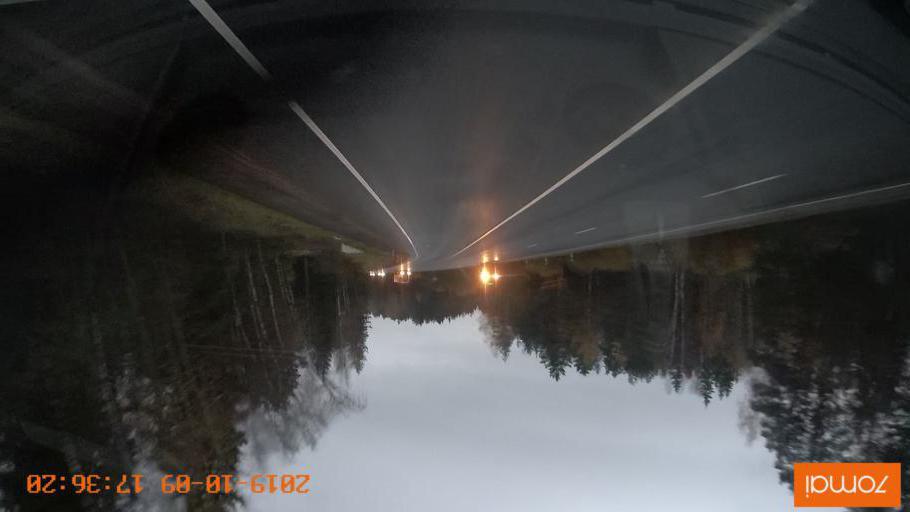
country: RU
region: Ivanovo
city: Bogorodskoye
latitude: 57.0799
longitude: 40.9978
